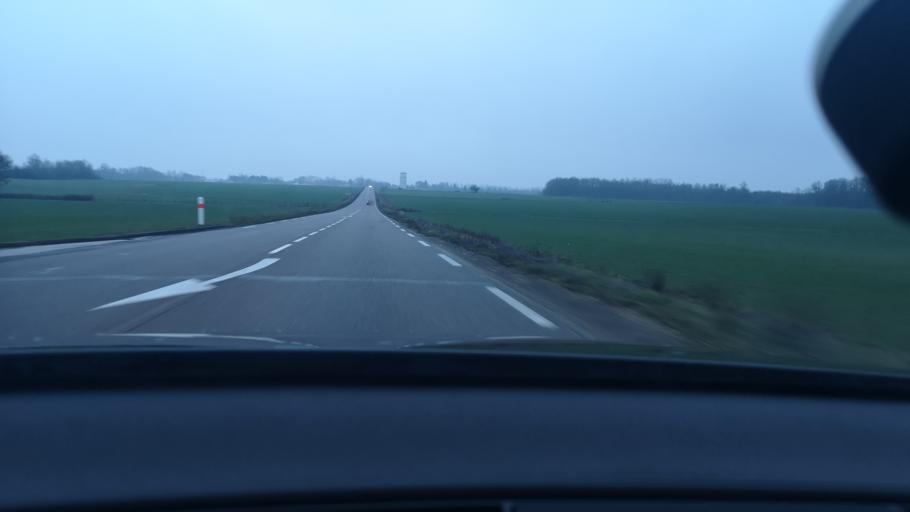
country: FR
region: Bourgogne
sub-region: Departement de la Cote-d'Or
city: Seurre
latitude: 47.0785
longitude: 5.1032
